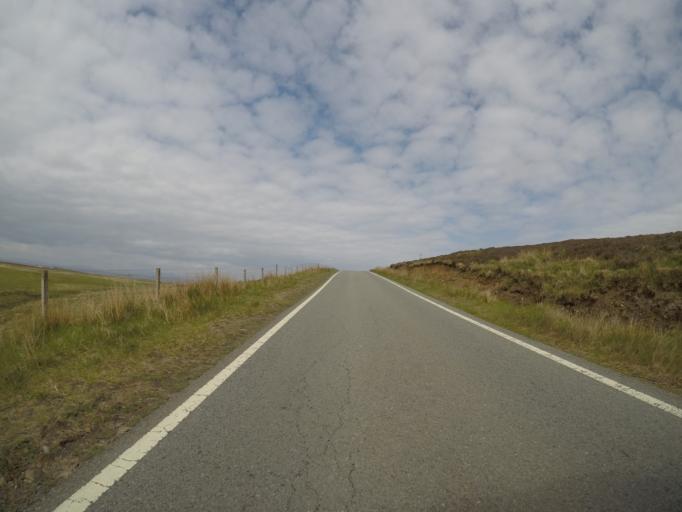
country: GB
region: Scotland
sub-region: Highland
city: Portree
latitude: 57.6518
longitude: -6.3802
